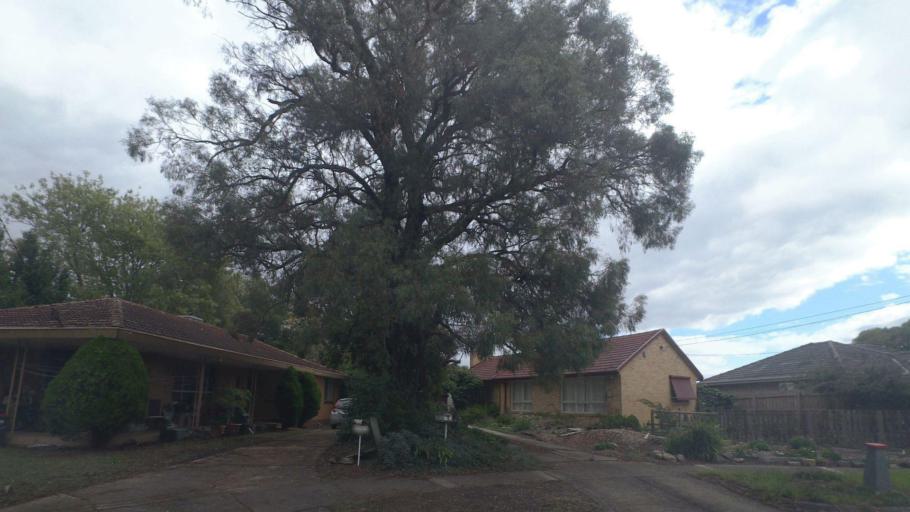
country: AU
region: Victoria
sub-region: Whitehorse
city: Forest Hill
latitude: -37.8301
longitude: 145.1703
